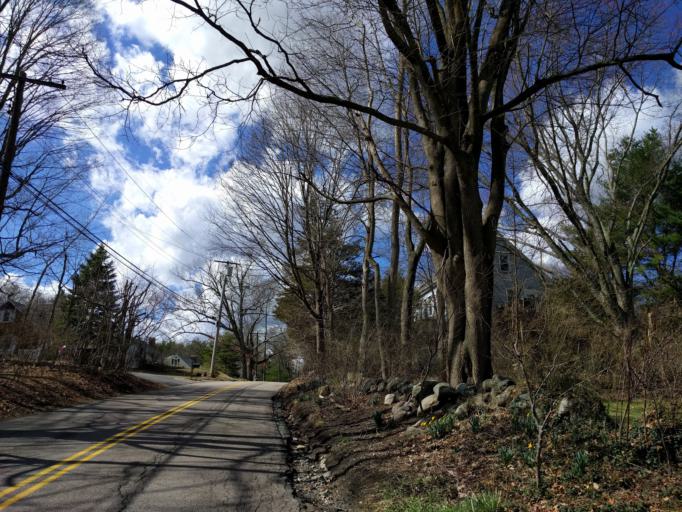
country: US
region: Massachusetts
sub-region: Norfolk County
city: Millis-Clicquot
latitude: 42.1454
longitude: -71.3537
